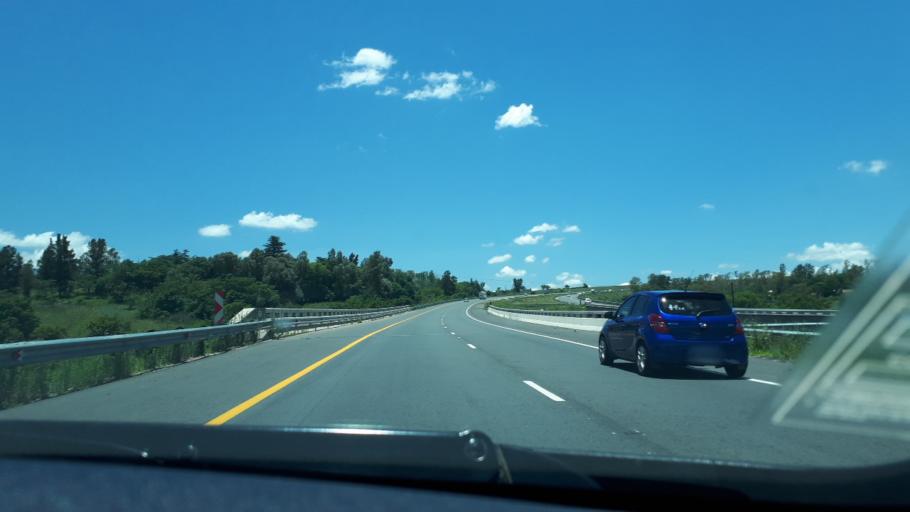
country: ZA
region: Gauteng
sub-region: City of Johannesburg Metropolitan Municipality
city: Diepsloot
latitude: -25.9489
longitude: 27.9566
